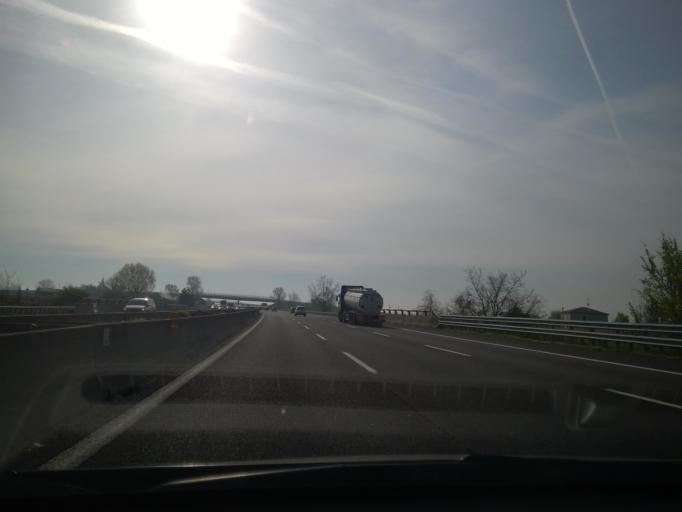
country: IT
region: Emilia-Romagna
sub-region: Provincia di Bologna
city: Mordano
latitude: 44.3619
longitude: 11.7904
